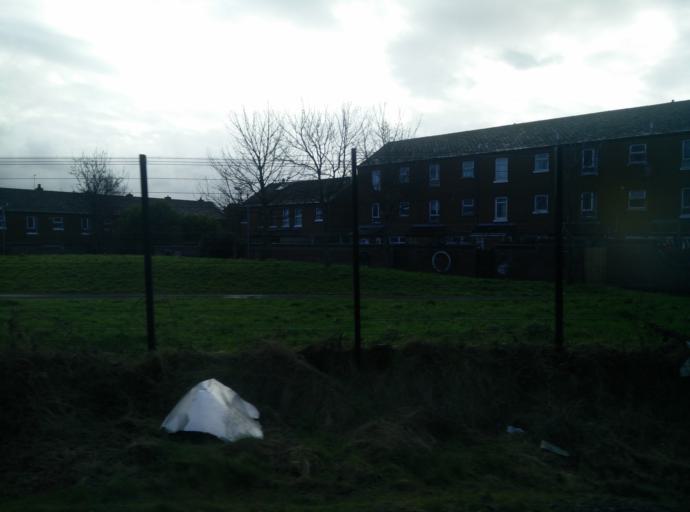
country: GB
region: Northern Ireland
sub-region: City of Belfast
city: Belfast
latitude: 54.5896
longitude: -5.9226
